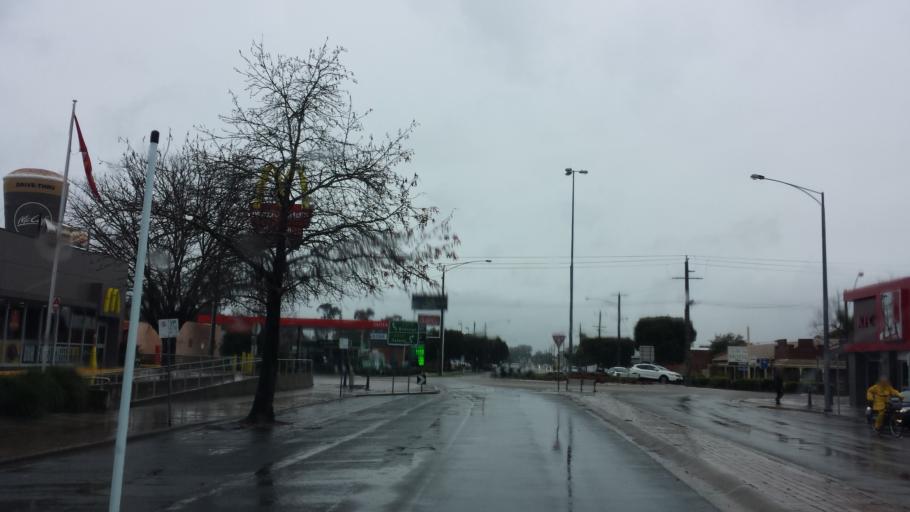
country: AU
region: Victoria
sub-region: Benalla
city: Benalla
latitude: -36.5508
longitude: 145.9876
